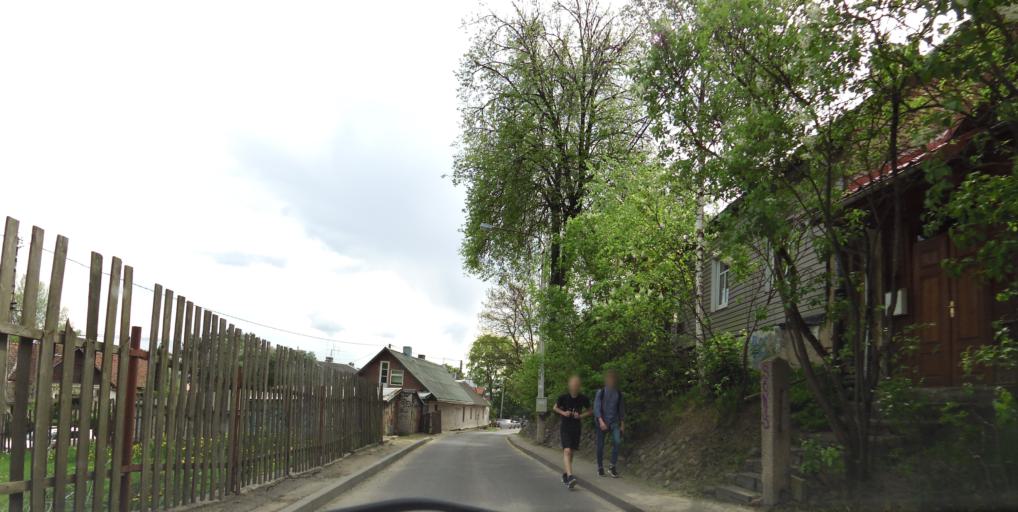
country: LT
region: Vilnius County
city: Rasos
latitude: 54.6840
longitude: 25.3033
